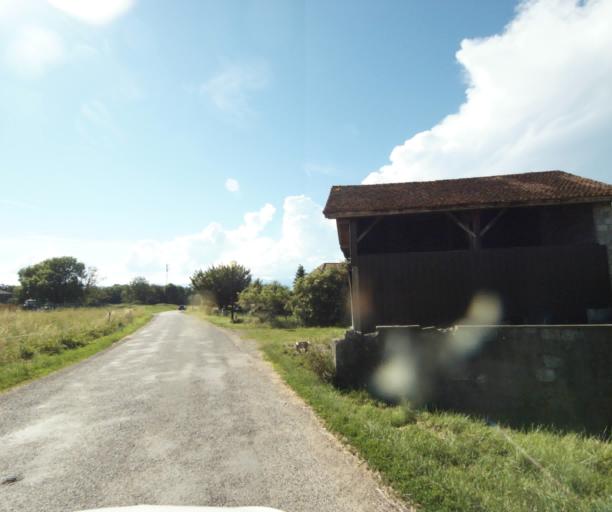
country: FR
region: Rhone-Alpes
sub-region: Departement de la Haute-Savoie
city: Massongy
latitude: 46.3244
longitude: 6.3189
